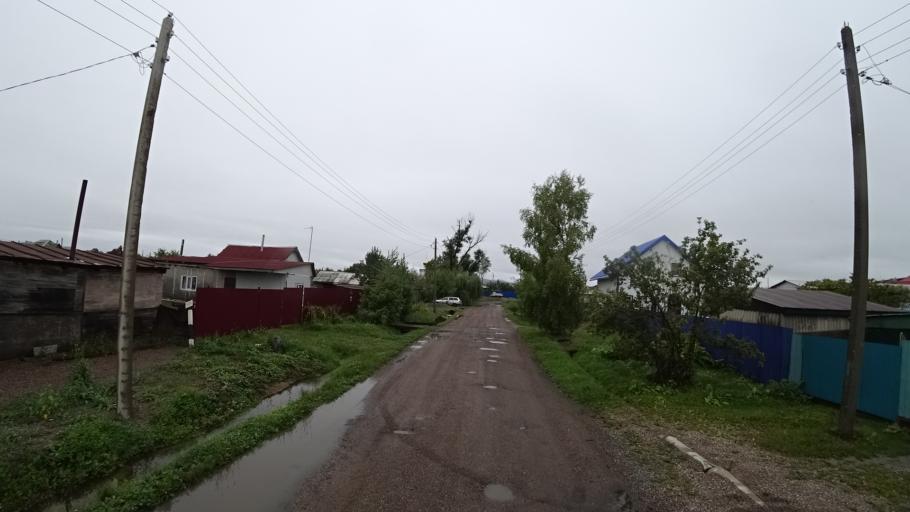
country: RU
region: Primorskiy
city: Monastyrishche
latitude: 44.2056
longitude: 132.4519
